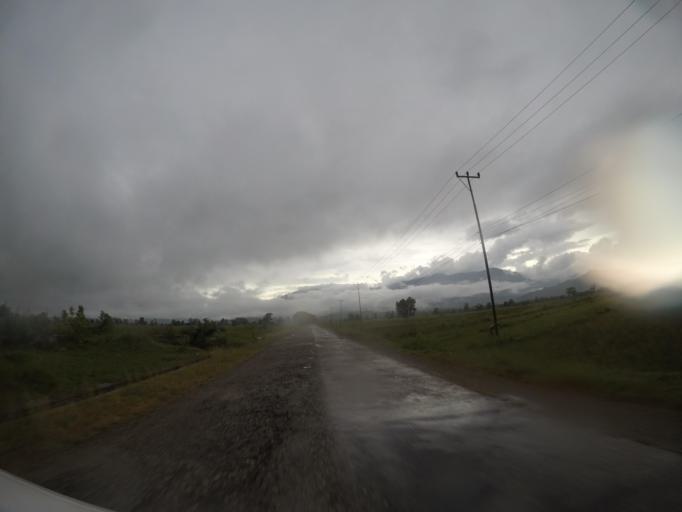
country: TL
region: Bobonaro
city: Maliana
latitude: -8.9871
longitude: 125.1642
